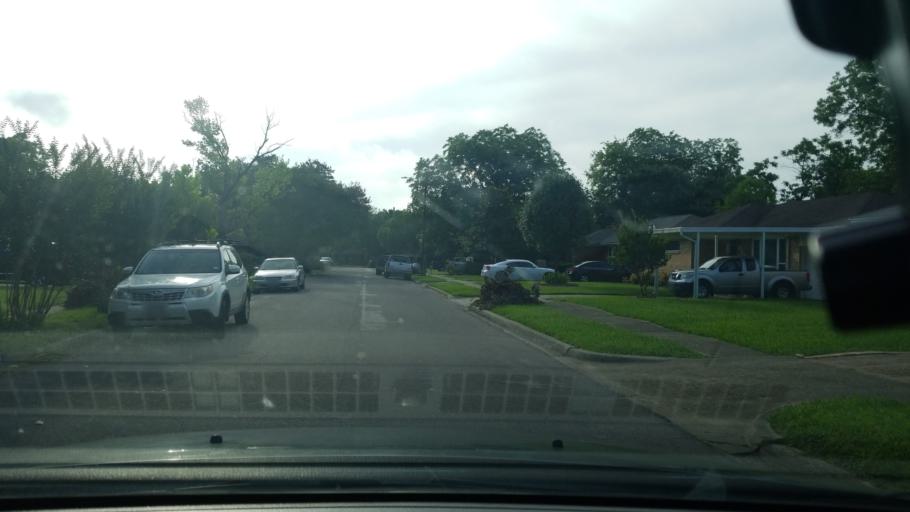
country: US
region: Texas
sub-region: Dallas County
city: Mesquite
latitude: 32.8286
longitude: -96.6596
